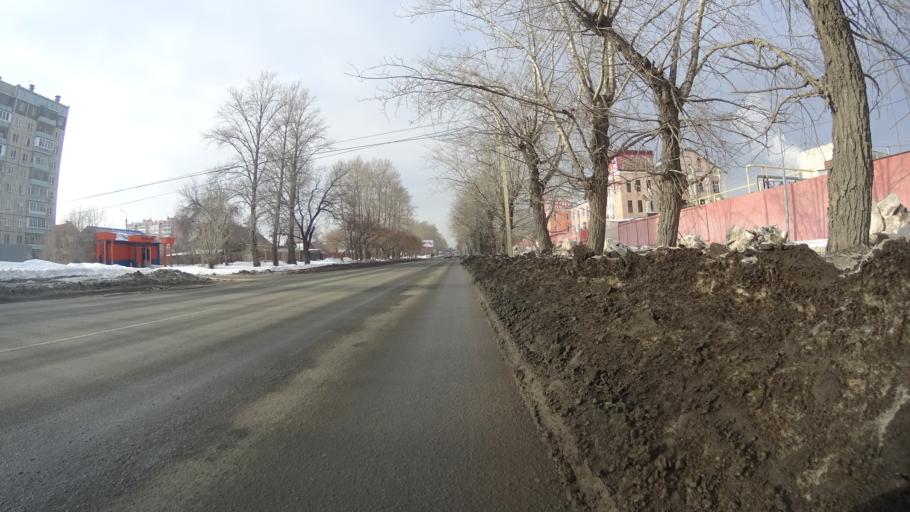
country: RU
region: Chelyabinsk
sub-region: Gorod Chelyabinsk
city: Chelyabinsk
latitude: 55.1227
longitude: 61.3755
